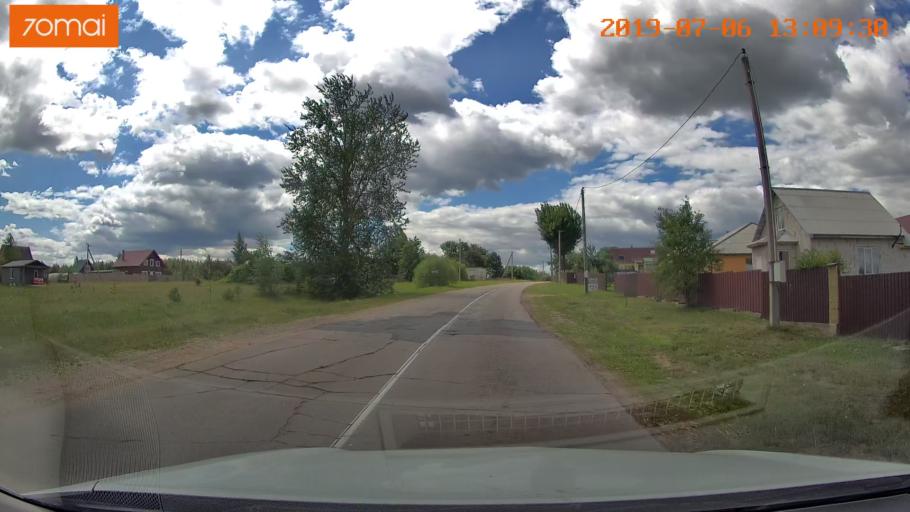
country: BY
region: Minsk
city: Enyerhyetykaw
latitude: 53.6616
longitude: 27.0120
